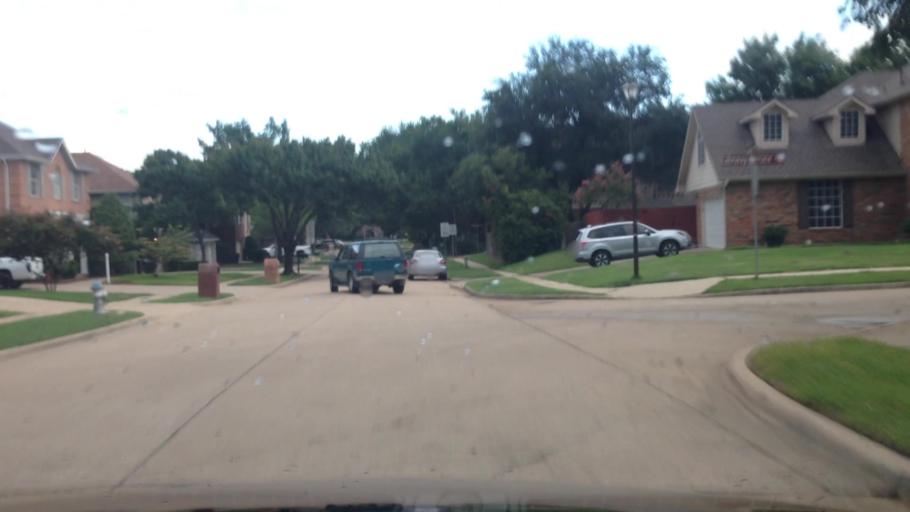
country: US
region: Texas
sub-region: Denton County
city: Flower Mound
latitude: 33.0194
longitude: -97.0639
